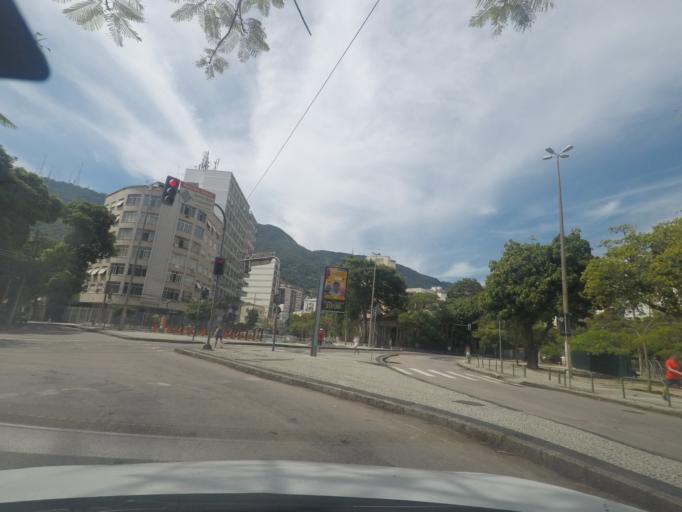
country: BR
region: Rio de Janeiro
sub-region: Rio De Janeiro
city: Rio de Janeiro
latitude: -22.9319
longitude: -43.2428
